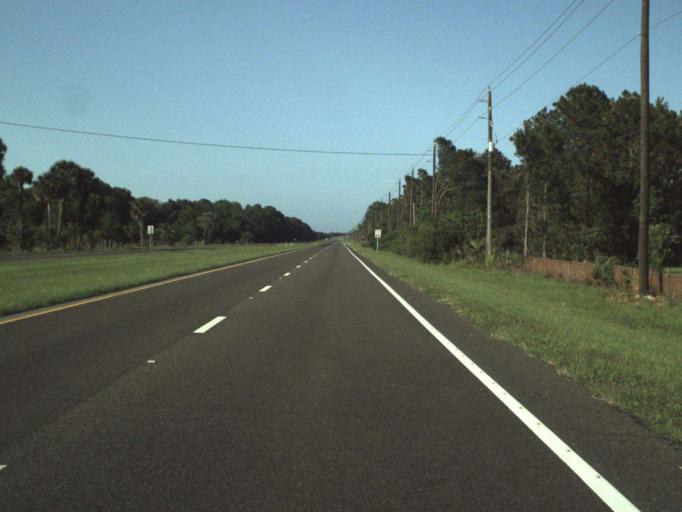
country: US
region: Florida
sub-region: Volusia County
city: Oak Hill
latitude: 28.8093
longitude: -80.8702
